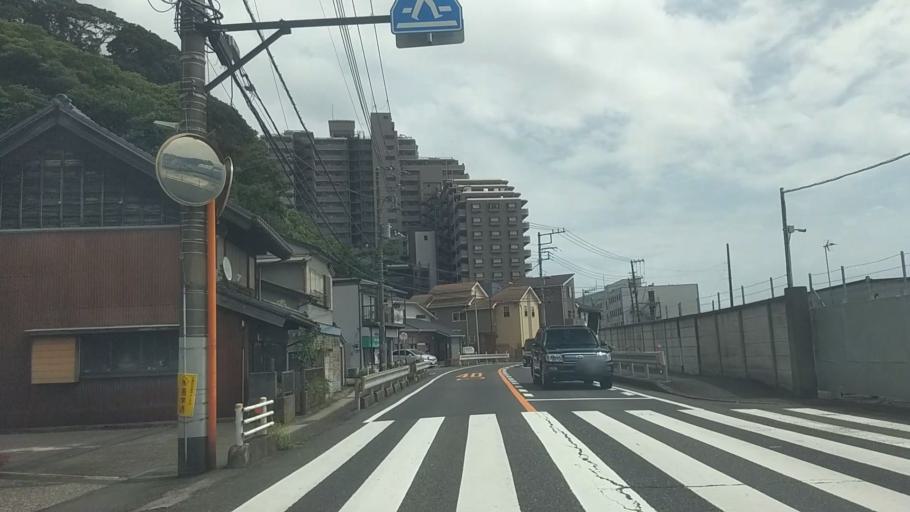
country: JP
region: Kanagawa
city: Yokosuka
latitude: 35.2474
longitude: 139.7185
